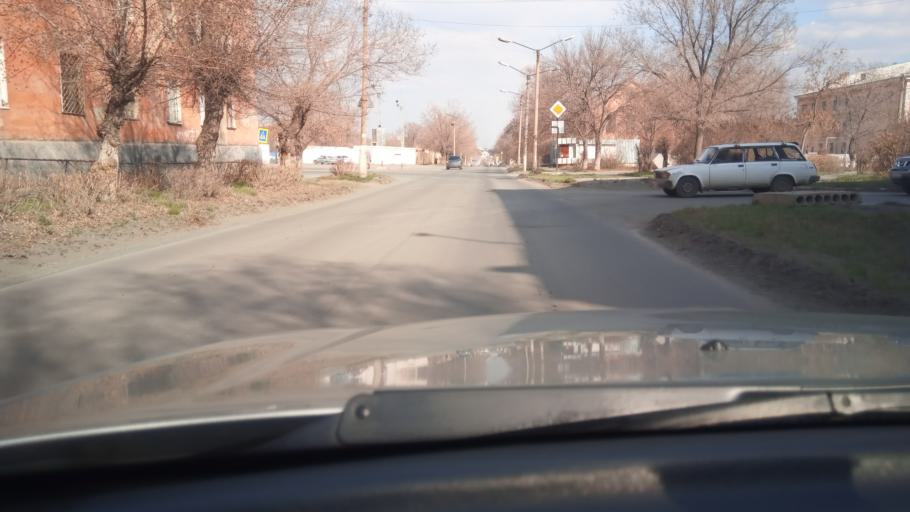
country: RU
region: Orenburg
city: Novotroitsk
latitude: 51.2034
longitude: 58.3029
